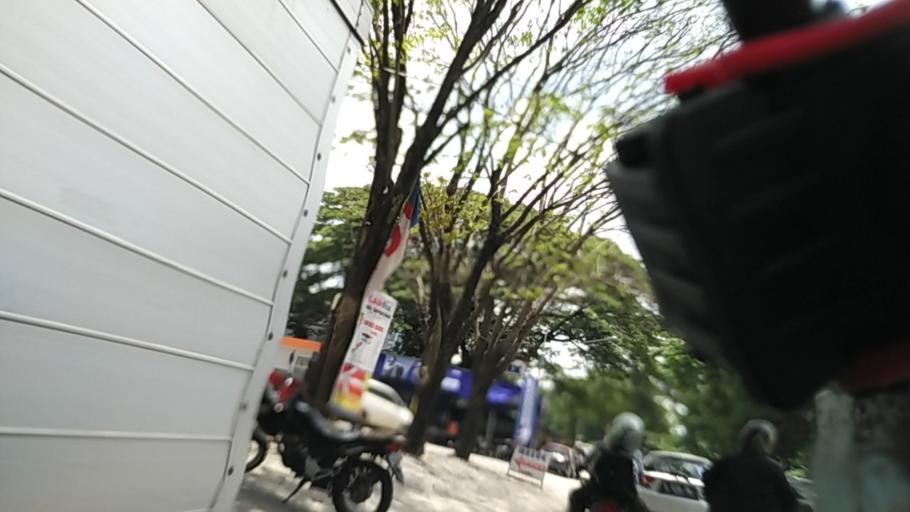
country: ID
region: Central Java
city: Semarang
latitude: -6.9888
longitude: 110.3853
